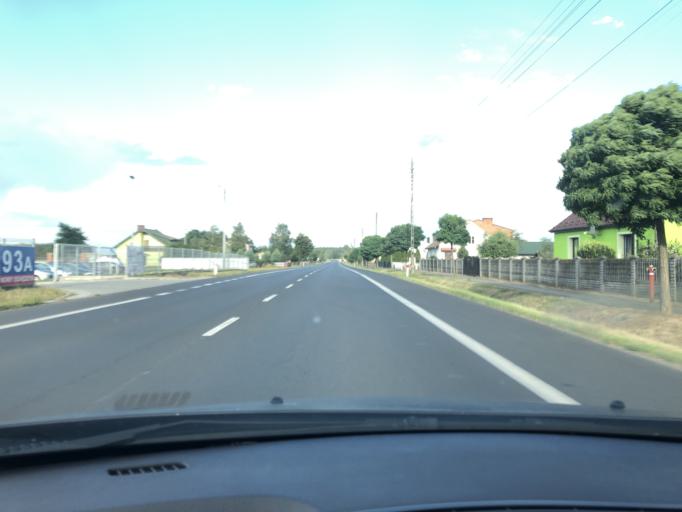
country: PL
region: Lodz Voivodeship
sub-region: Powiat wieruszowski
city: Galewice
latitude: 51.3041
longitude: 18.2459
